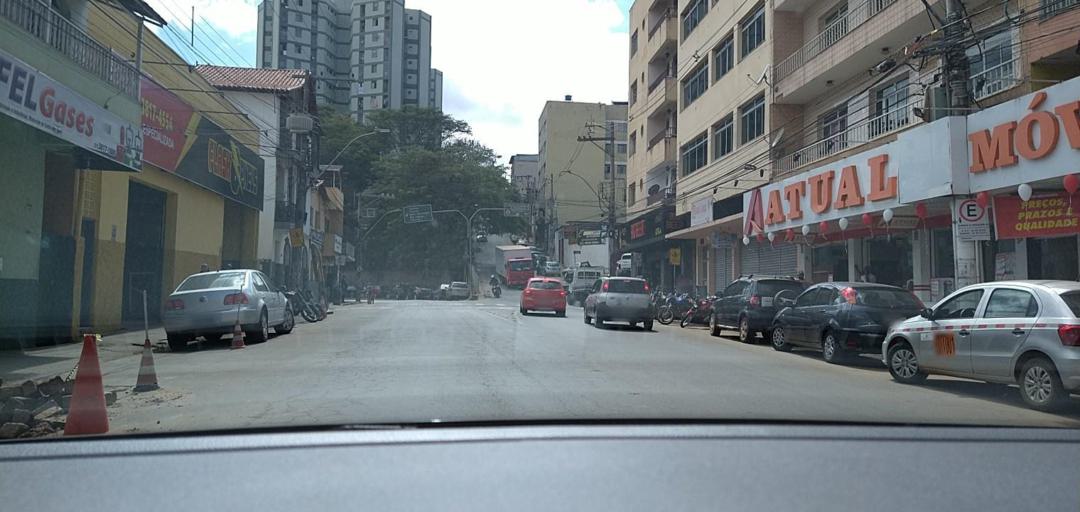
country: BR
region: Minas Gerais
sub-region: Ponte Nova
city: Ponte Nova
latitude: -20.4145
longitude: -42.8991
